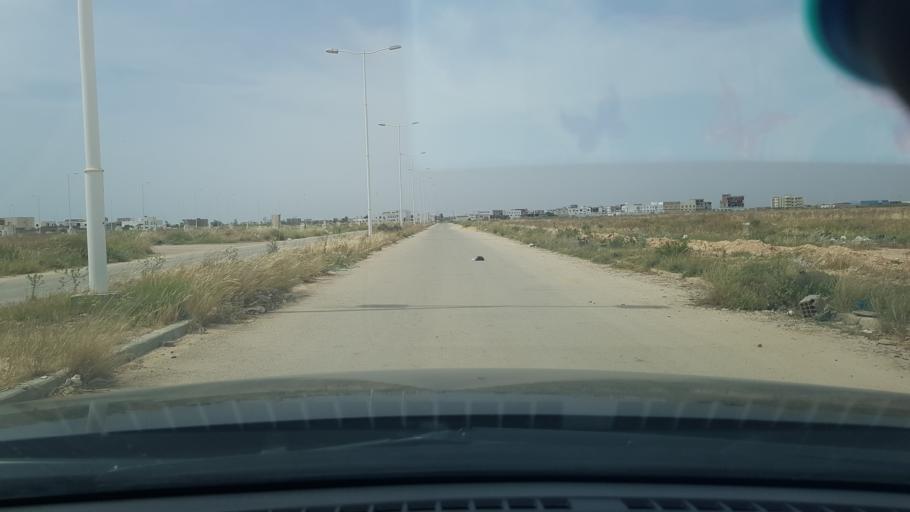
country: TN
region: Safaqis
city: Al Qarmadah
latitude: 34.8300
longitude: 10.7490
